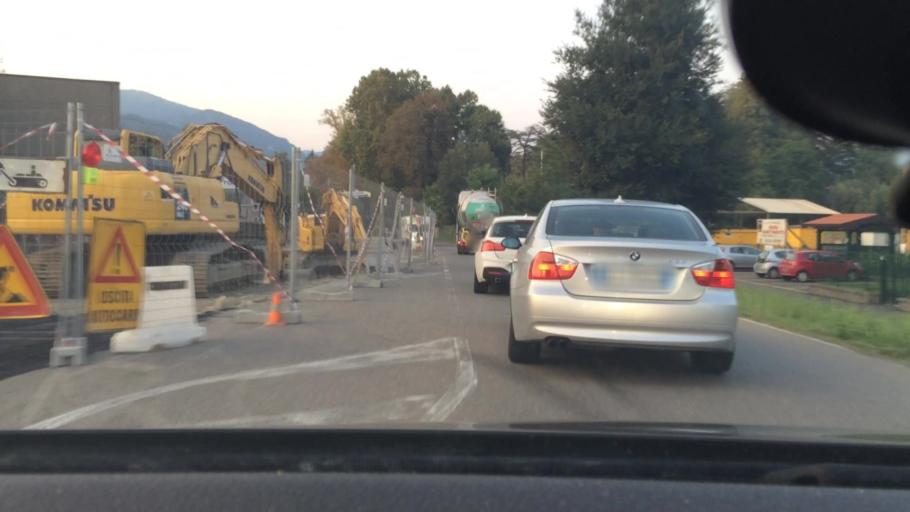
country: IT
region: Lombardy
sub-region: Provincia di Como
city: Alserio
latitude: 45.7877
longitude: 9.1966
